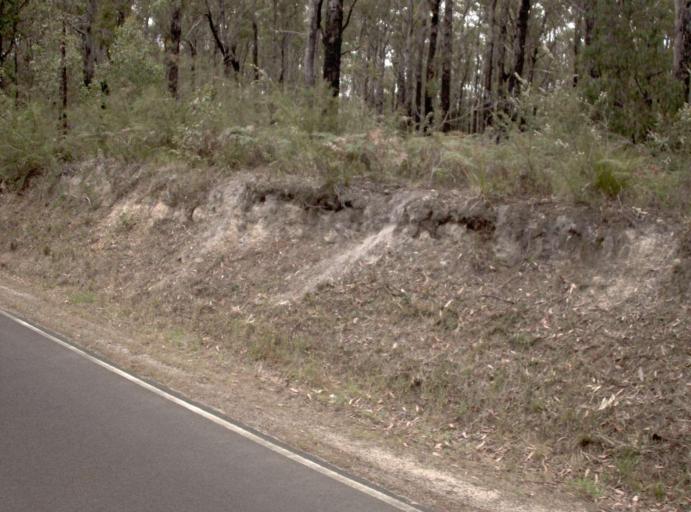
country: AU
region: Victoria
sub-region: Latrobe
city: Traralgon
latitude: -38.4743
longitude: 146.8224
